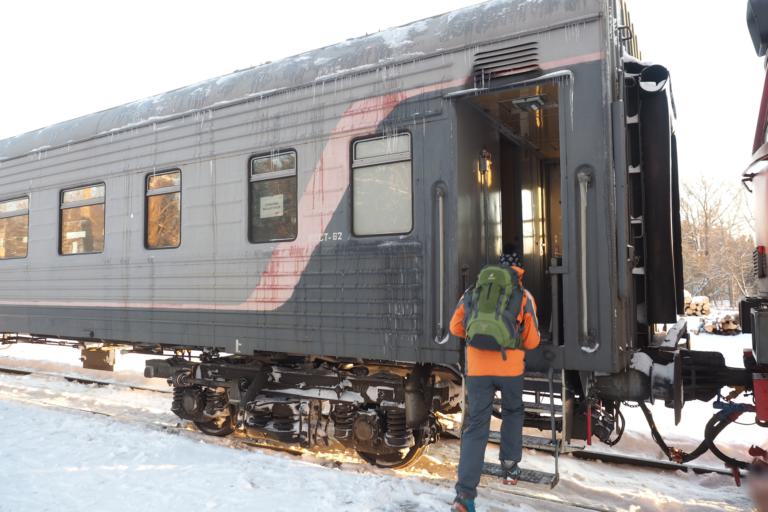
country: RU
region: Tverskaya
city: Ves'yegonsk
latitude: 58.6539
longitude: 37.2641
